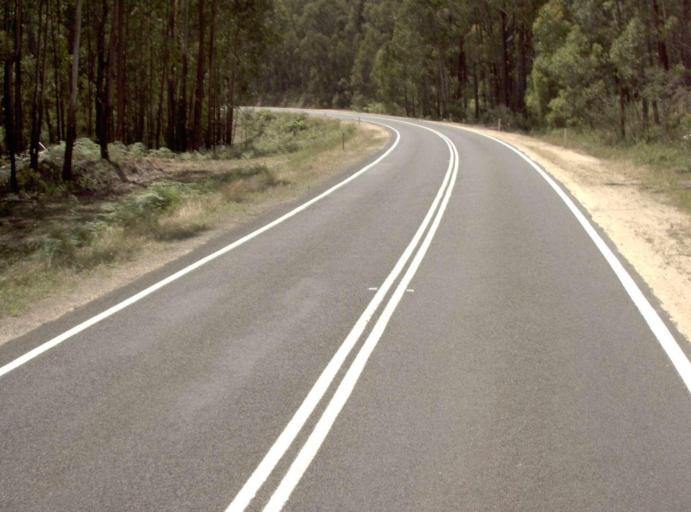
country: AU
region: New South Wales
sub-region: Bombala
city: Bombala
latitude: -37.5641
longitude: 149.2512
